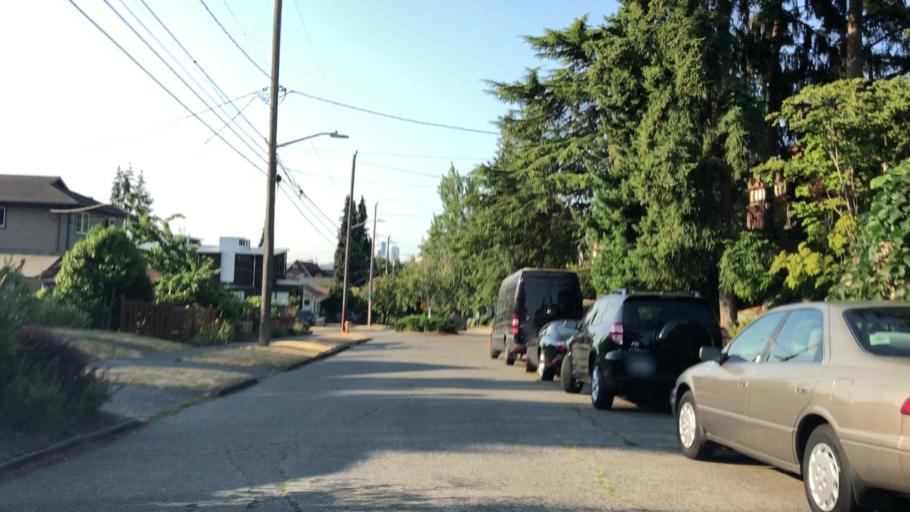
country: US
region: Washington
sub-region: King County
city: Seattle
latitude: 47.6574
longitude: -122.3338
